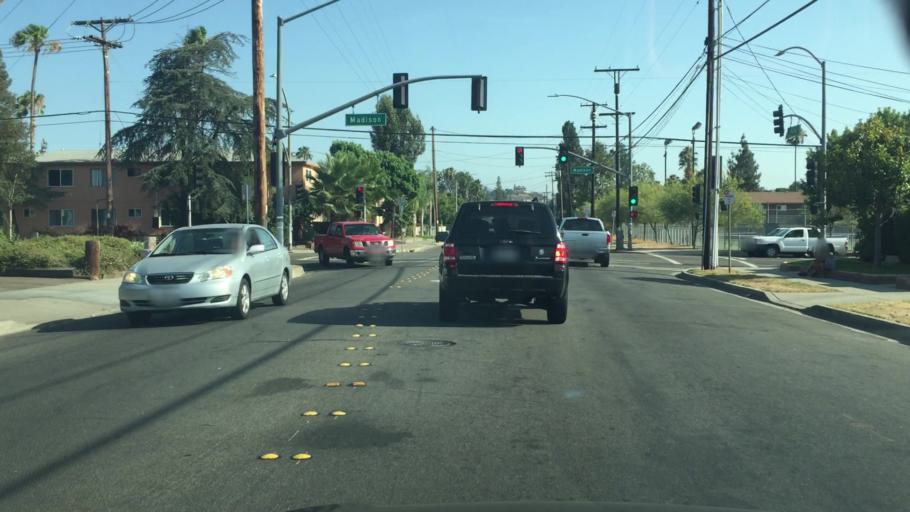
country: US
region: California
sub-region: San Diego County
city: Bostonia
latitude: 32.8006
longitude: -116.9446
